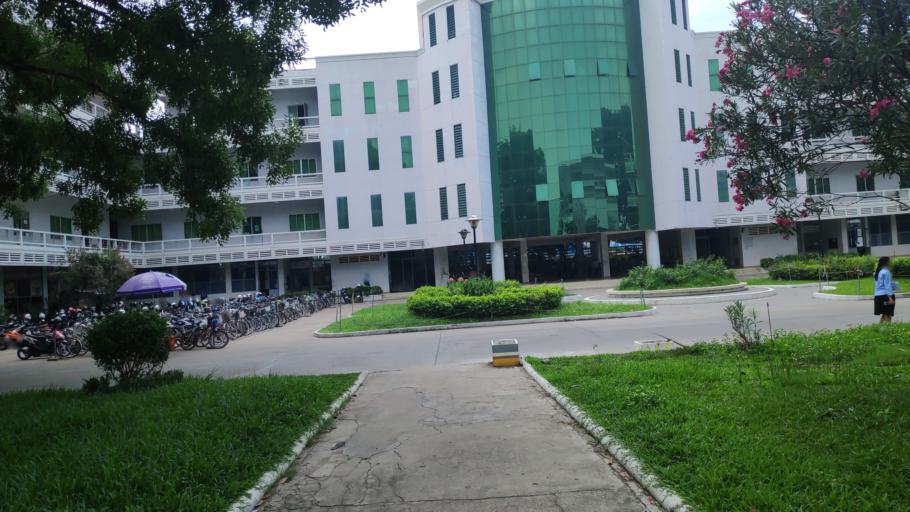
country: KH
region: Phnom Penh
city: Phnom Penh
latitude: 11.5709
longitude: 104.8989
